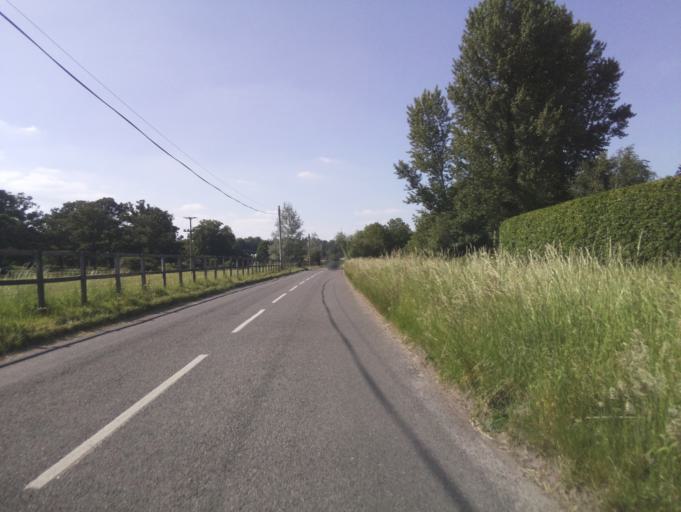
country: GB
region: England
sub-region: Hampshire
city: Abbotts Ann
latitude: 51.2401
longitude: -1.5677
